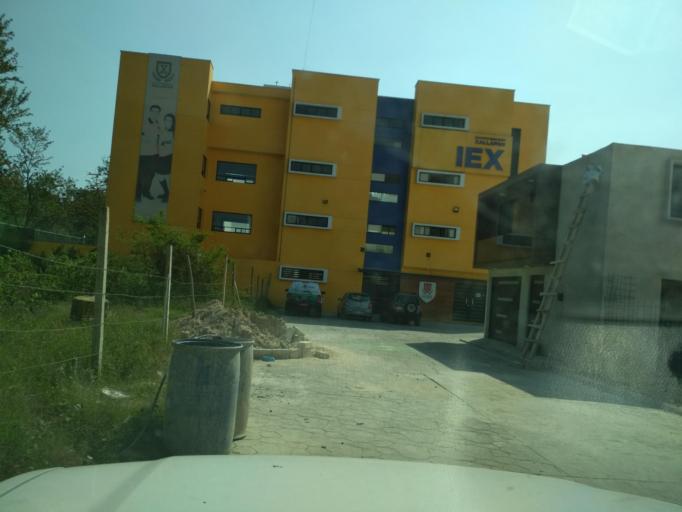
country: MX
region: Veracruz
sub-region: Emiliano Zapata
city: Las Trancas
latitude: 19.5164
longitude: -96.8591
